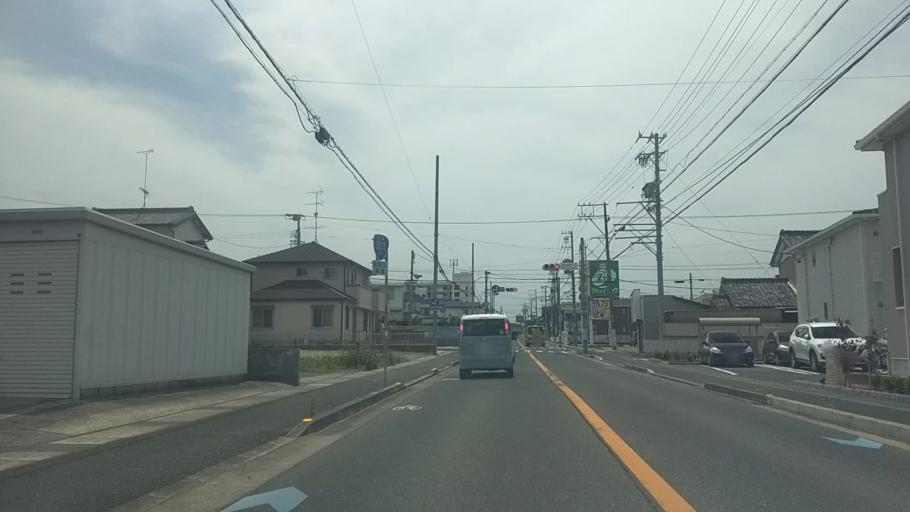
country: JP
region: Shizuoka
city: Kosai-shi
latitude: 34.7136
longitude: 137.5470
